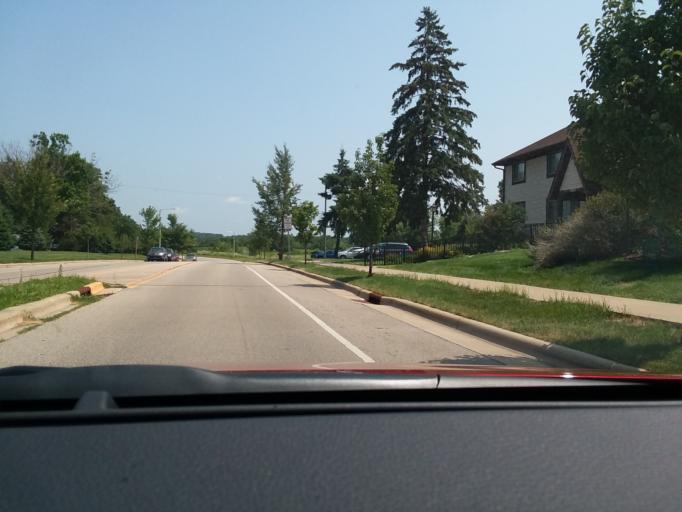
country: US
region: Wisconsin
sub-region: Dane County
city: Madison
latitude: 43.0261
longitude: -89.4118
